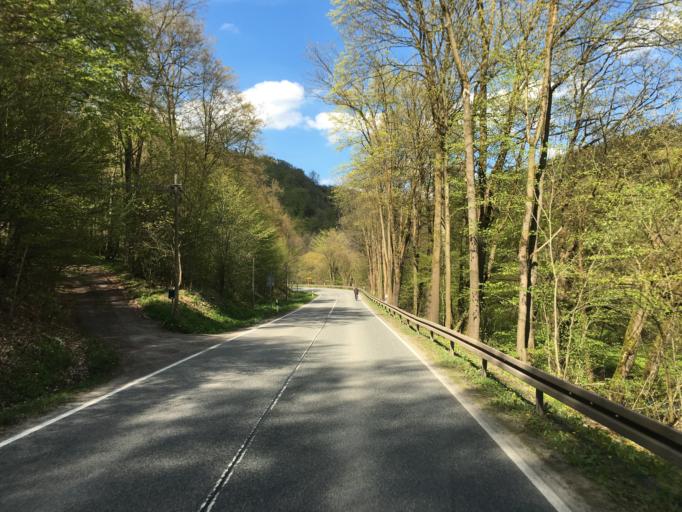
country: DE
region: Thuringia
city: Ilfeld
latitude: 51.6003
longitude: 10.7853
